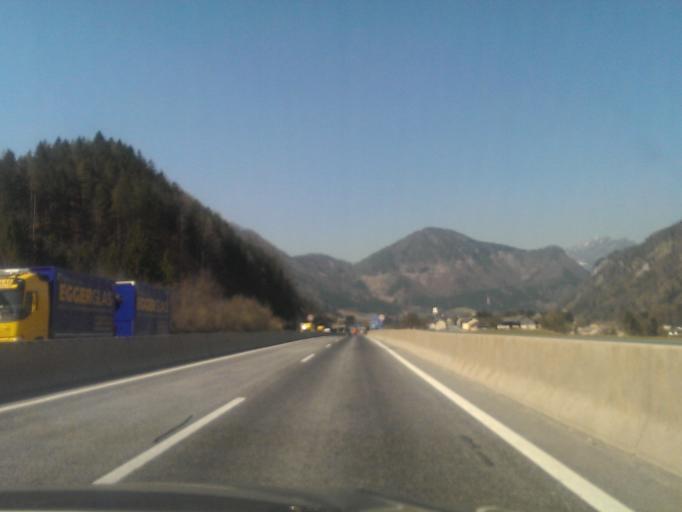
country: AT
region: Upper Austria
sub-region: Politischer Bezirk Kirchdorf an der Krems
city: Rossleithen
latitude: 47.7674
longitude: 14.1871
